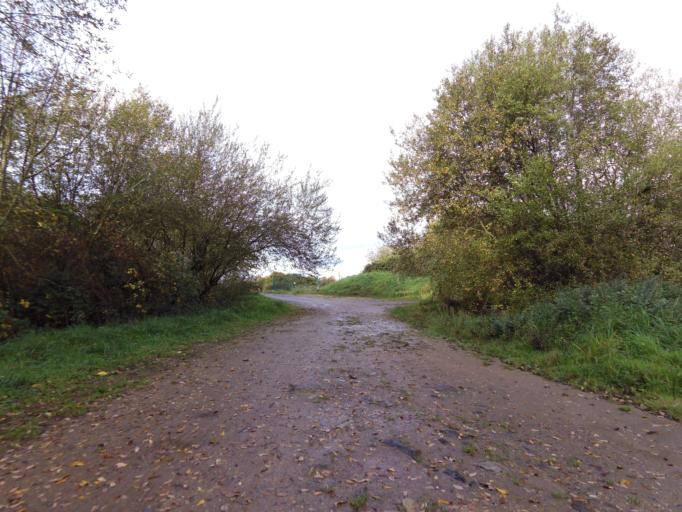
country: FR
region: Brittany
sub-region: Departement d'Ille-et-Vilaine
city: Bourg-des-Comptes
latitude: 47.9361
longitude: -1.7542
